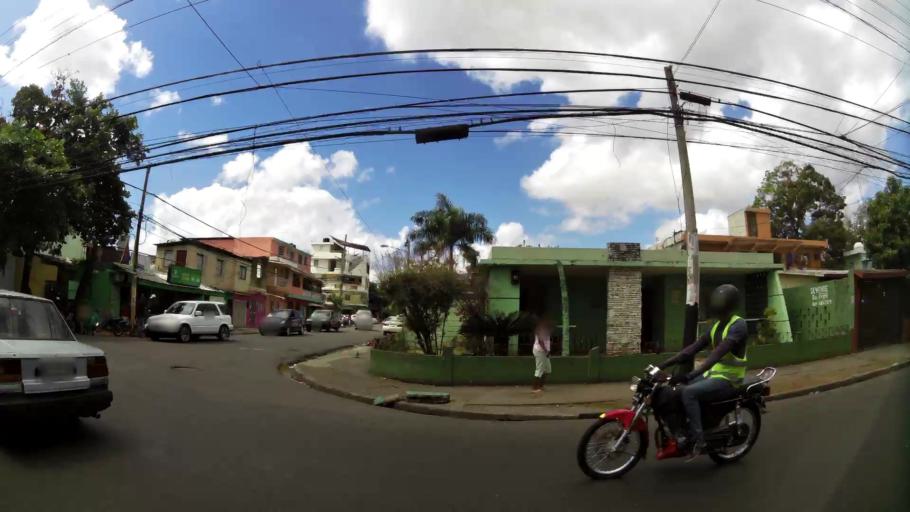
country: DO
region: Nacional
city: Ensanche Luperon
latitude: 18.5007
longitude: -69.8938
